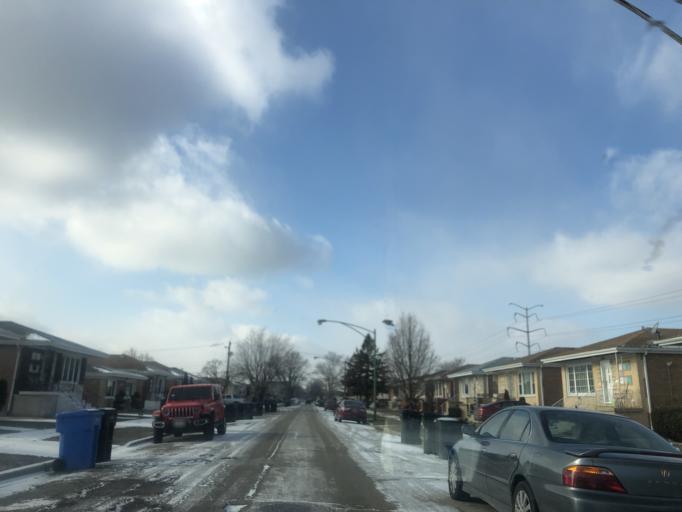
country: US
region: Illinois
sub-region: Cook County
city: Hometown
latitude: 41.7565
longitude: -87.7151
